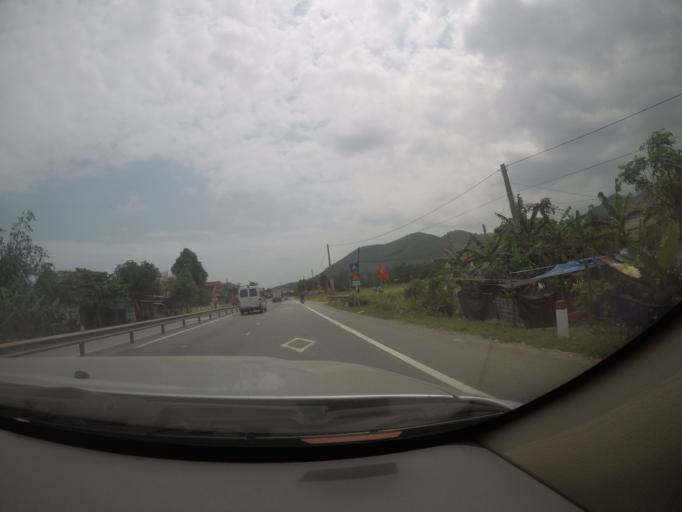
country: VN
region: Thua Thien-Hue
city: Phu Loc
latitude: 16.2880
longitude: 107.8363
